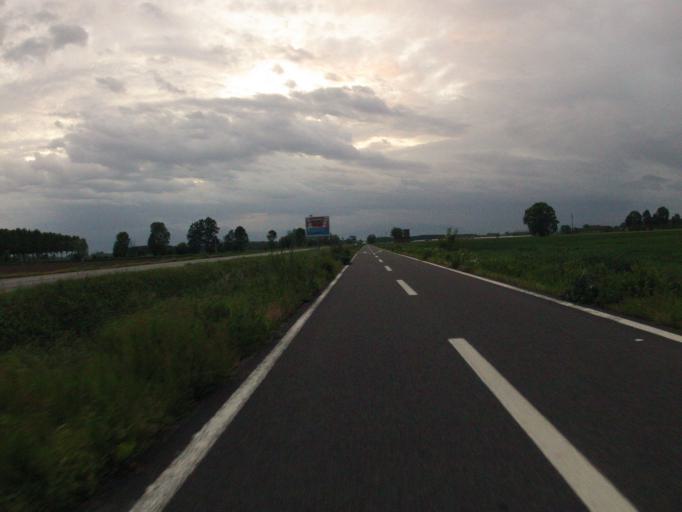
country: IT
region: Piedmont
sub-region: Provincia di Cuneo
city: Moretta
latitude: 44.7700
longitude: 7.5269
